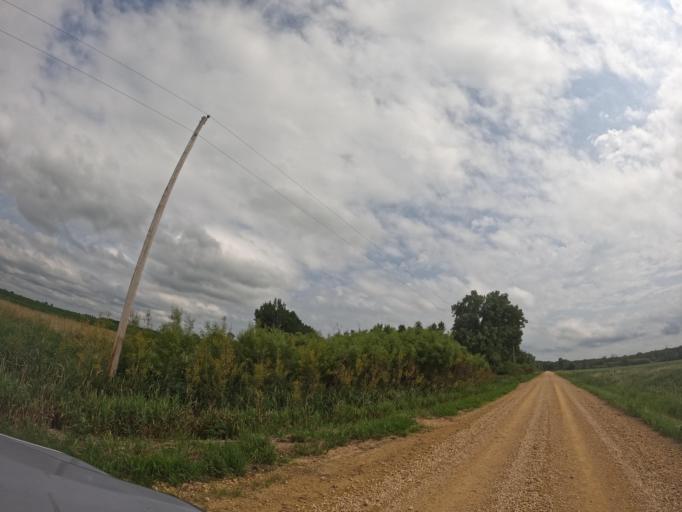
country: US
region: Iowa
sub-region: Clinton County
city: De Witt
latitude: 41.7772
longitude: -90.5827
